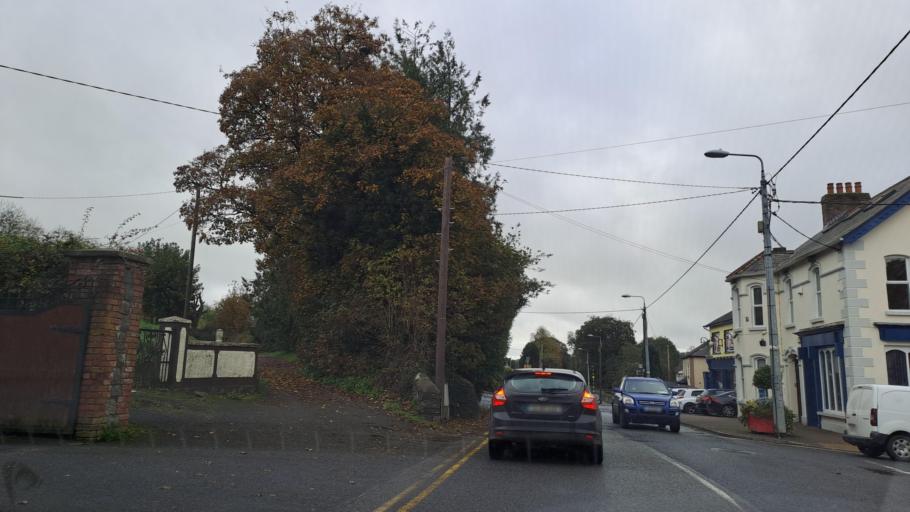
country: IE
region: Ulster
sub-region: An Cabhan
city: Bailieborough
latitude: 53.9149
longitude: -6.9700
